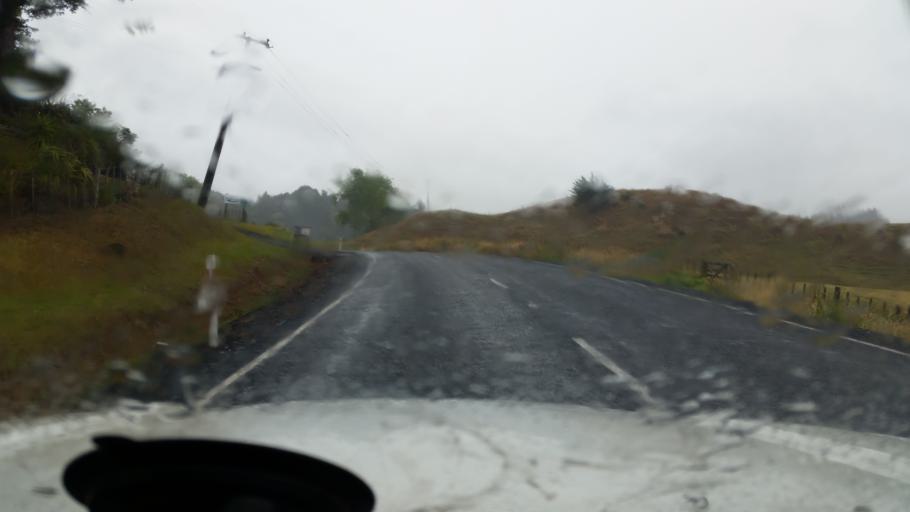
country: NZ
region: Northland
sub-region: Far North District
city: Kaitaia
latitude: -35.2745
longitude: 173.3507
